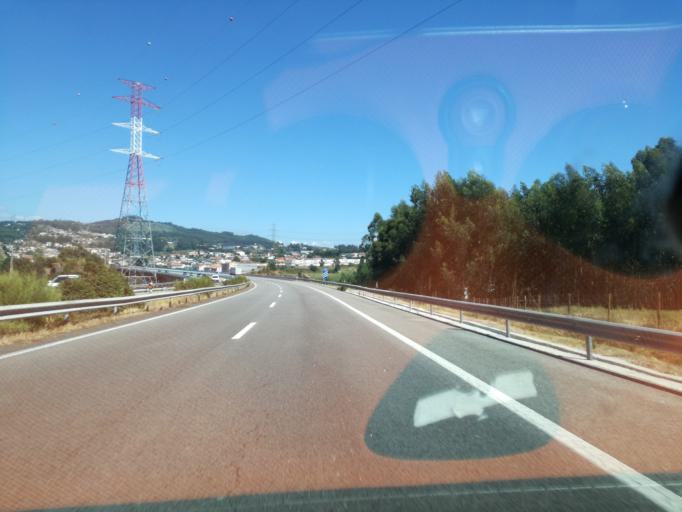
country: PT
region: Braga
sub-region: Guimaraes
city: Serzedelo
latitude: 41.4054
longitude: -8.3880
